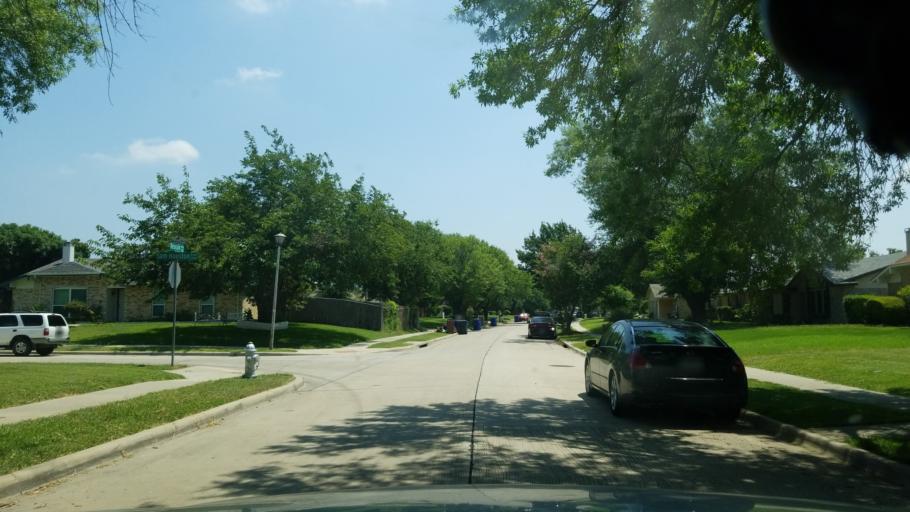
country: US
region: Texas
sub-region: Dallas County
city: Carrollton
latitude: 32.9517
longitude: -96.8806
